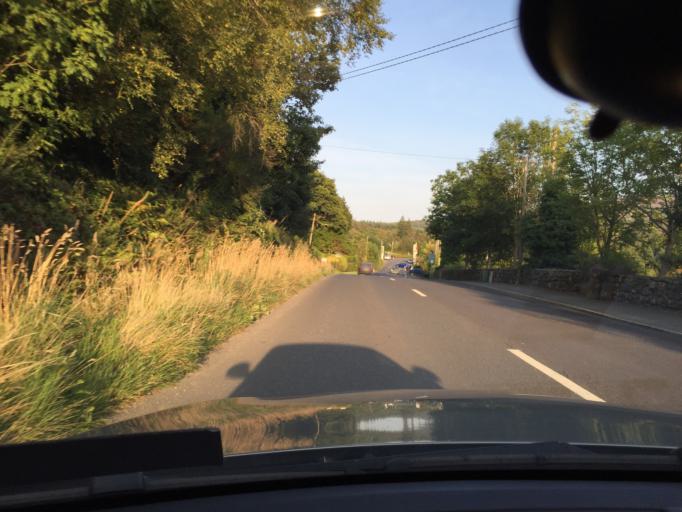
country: IE
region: Leinster
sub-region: Wicklow
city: Rathdrum
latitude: 53.0091
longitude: -6.3027
